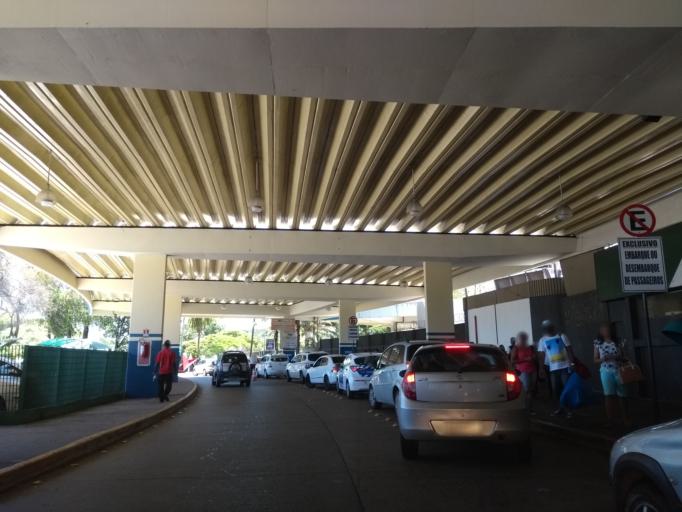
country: BR
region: Bahia
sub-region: Salvador
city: Salvador
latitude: -12.9783
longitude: -38.4657
